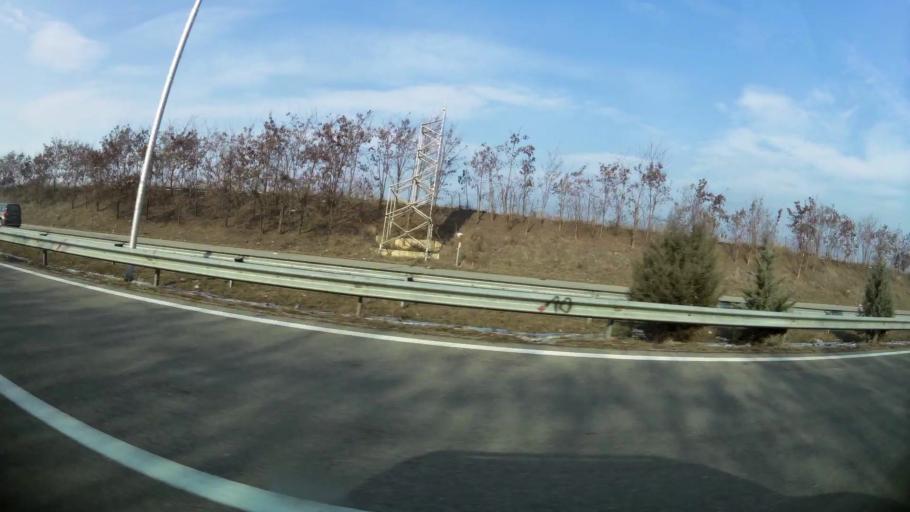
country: MK
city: Creshevo
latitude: 42.0341
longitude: 21.5207
